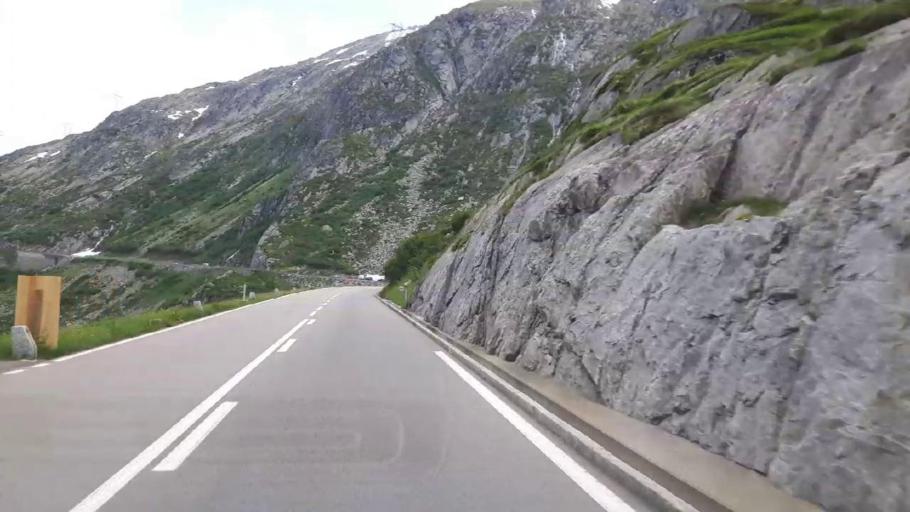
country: CH
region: Uri
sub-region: Uri
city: Andermatt
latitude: 46.5924
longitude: 8.5607
